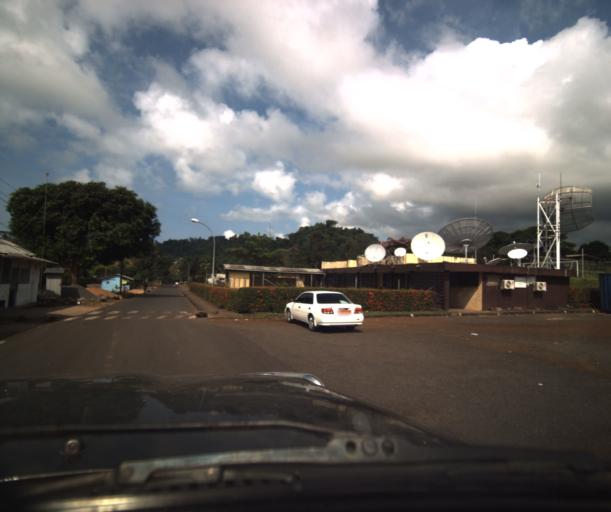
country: CM
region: South-West Province
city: Limbe
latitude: 4.0192
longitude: 9.1872
